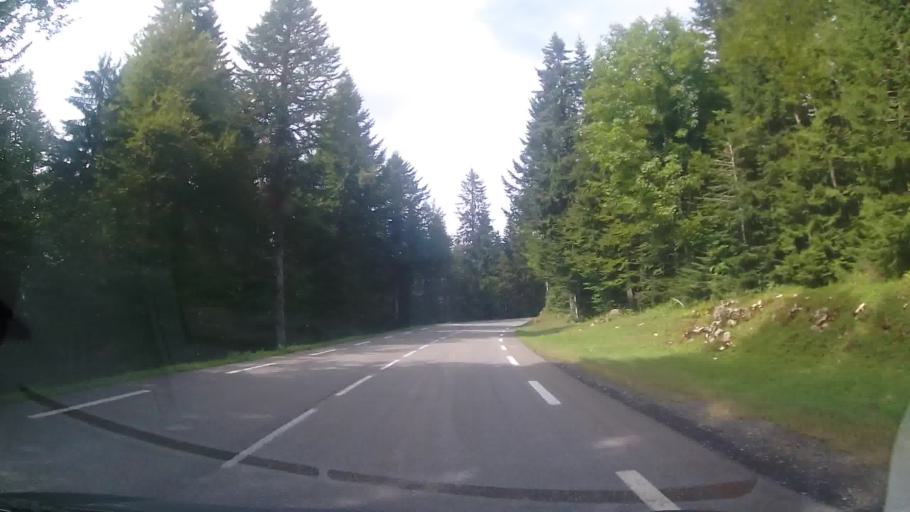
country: FR
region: Rhone-Alpes
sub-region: Departement de l'Ain
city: Gex
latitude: 46.3903
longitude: 6.0490
